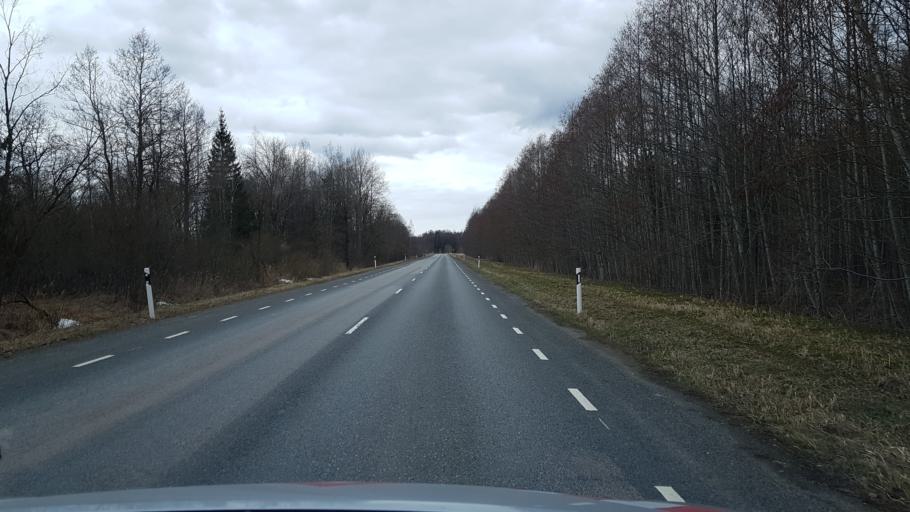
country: EE
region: Ida-Virumaa
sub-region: Narva-Joesuu linn
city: Narva-Joesuu
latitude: 59.3513
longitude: 28.0514
